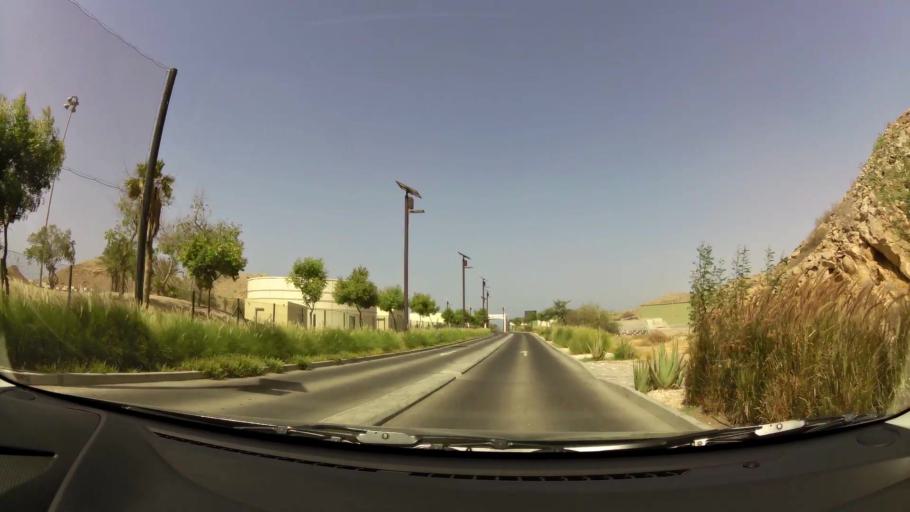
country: OM
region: Muhafazat Masqat
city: Muscat
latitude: 23.6369
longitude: 58.5042
